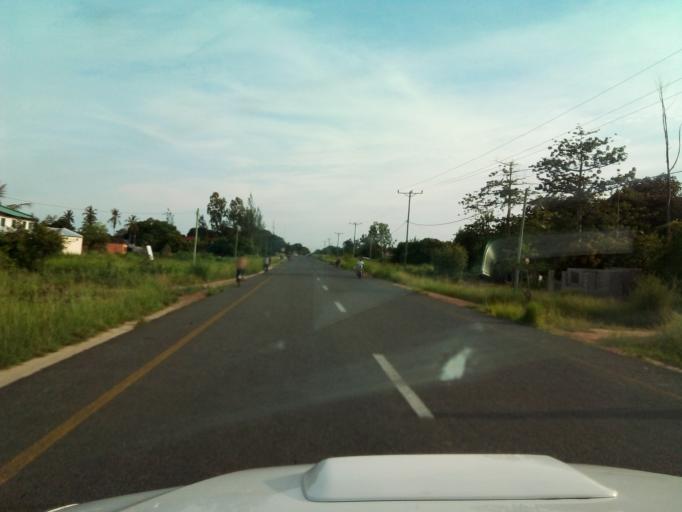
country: MZ
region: Zambezia
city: Quelimane
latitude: -17.4824
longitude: 37.0304
